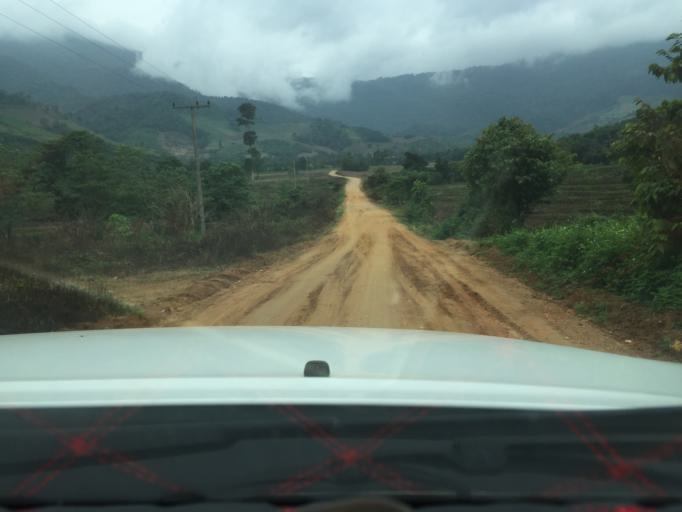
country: TH
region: Phayao
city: Phu Sang
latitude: 19.7417
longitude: 100.4402
